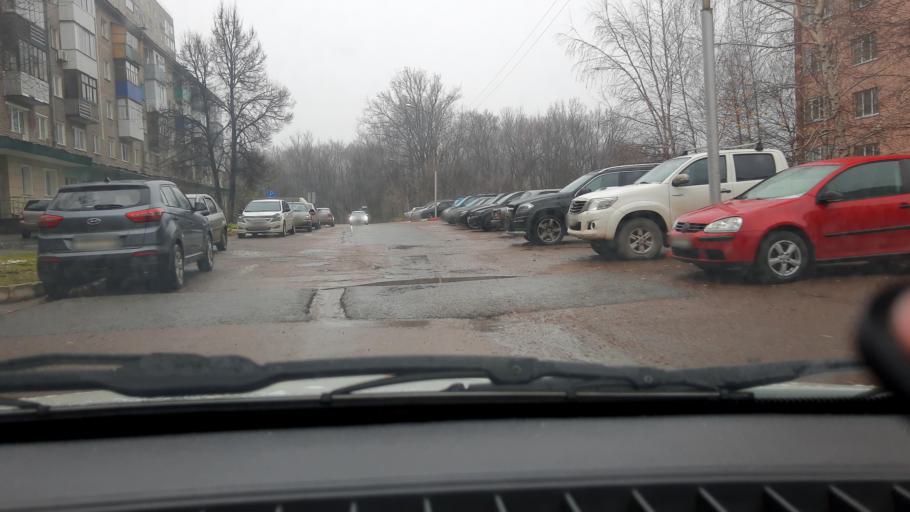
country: RU
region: Bashkortostan
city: Ufa
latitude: 54.7631
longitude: 55.9919
